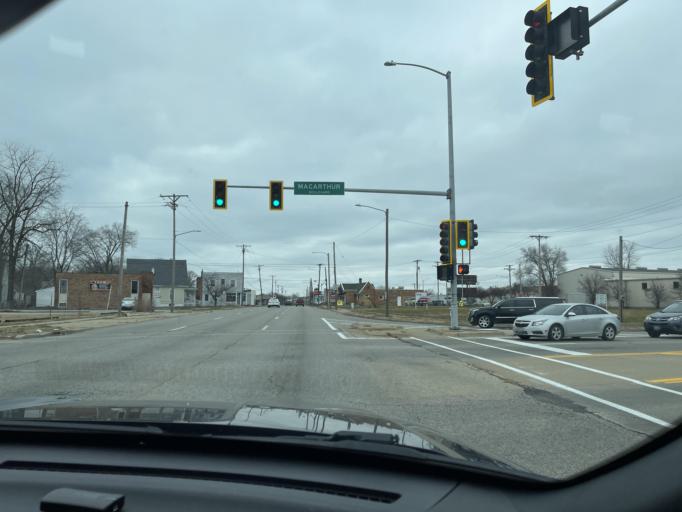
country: US
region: Illinois
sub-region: Sangamon County
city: Springfield
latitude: 39.8046
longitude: -89.6682
